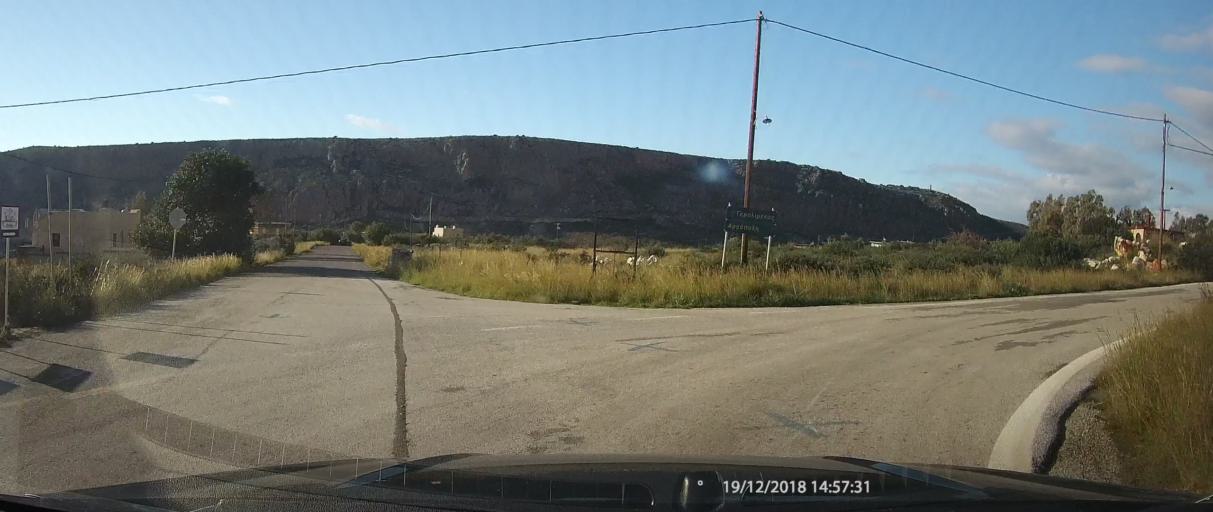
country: GR
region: Peloponnese
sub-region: Nomos Lakonias
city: Gytheio
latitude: 36.4806
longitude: 22.4052
